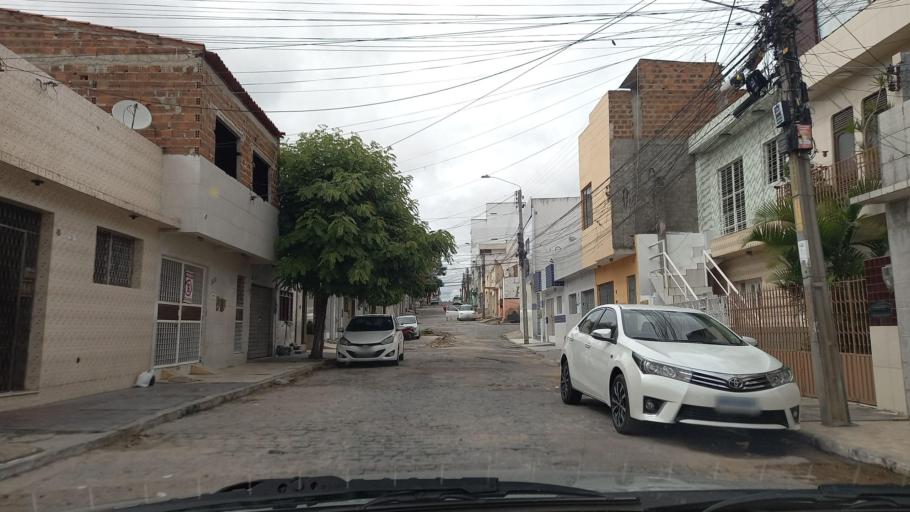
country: BR
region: Pernambuco
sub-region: Caruaru
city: Caruaru
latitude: -8.2775
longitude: -35.9775
